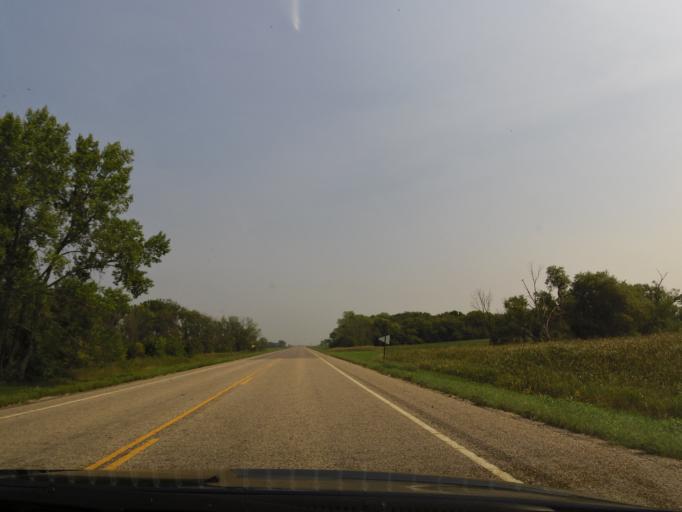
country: US
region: South Dakota
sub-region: Roberts County
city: Sisseton
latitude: 45.8488
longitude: -97.0059
